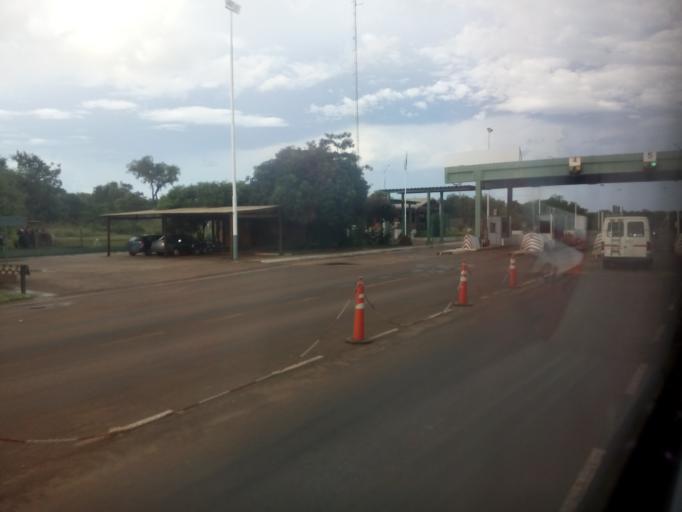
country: AR
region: Misiones
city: Santa Ana
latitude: -27.4288
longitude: -55.6301
